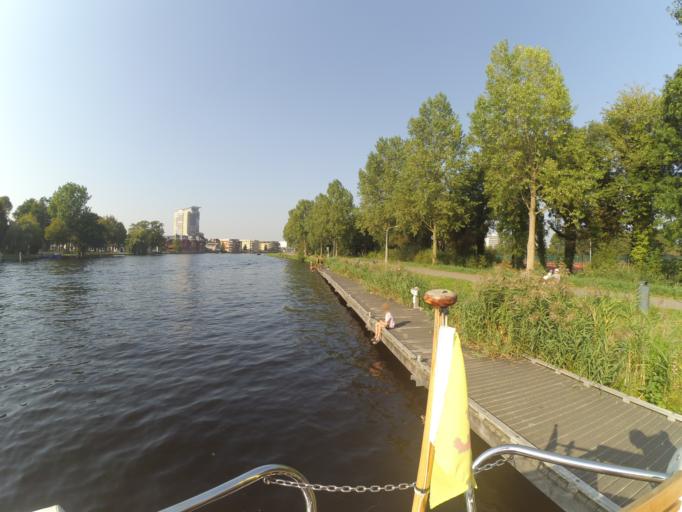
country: NL
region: North Holland
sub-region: Gemeente Haarlem
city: Haarlem
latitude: 52.3666
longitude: 4.6372
